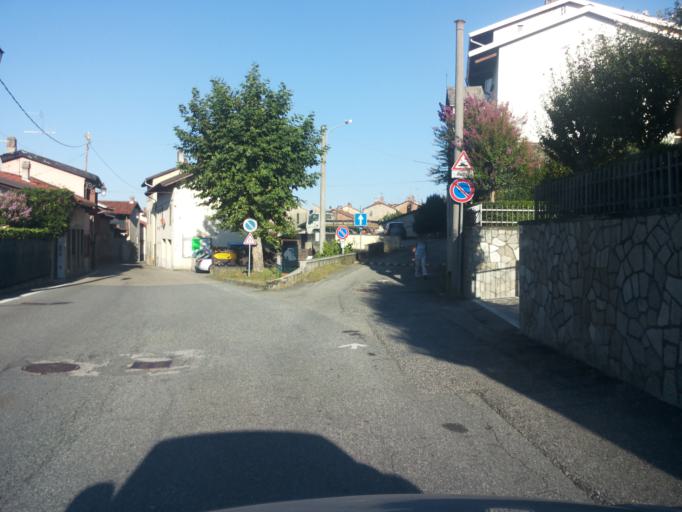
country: IT
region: Piedmont
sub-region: Provincia di Torino
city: Caravino
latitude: 45.3975
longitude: 7.9580
